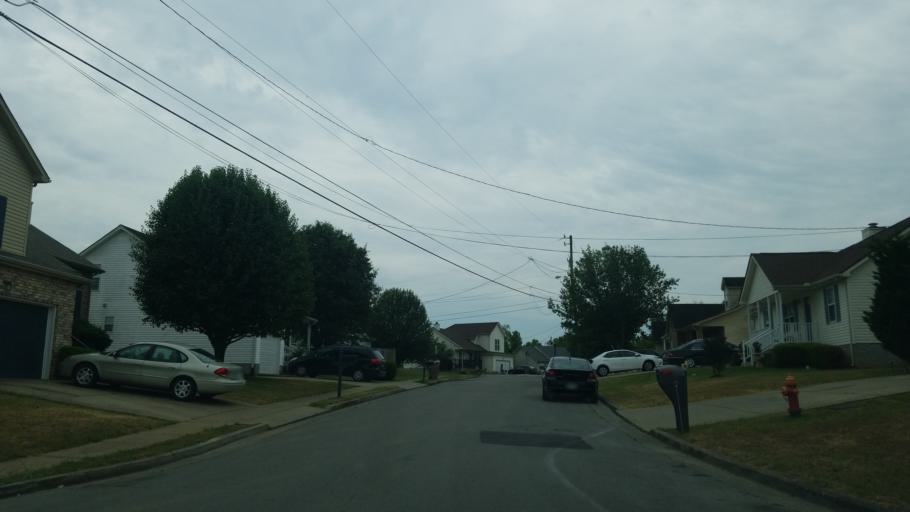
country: US
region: Tennessee
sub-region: Rutherford County
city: La Vergne
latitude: 36.0444
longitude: -86.5905
